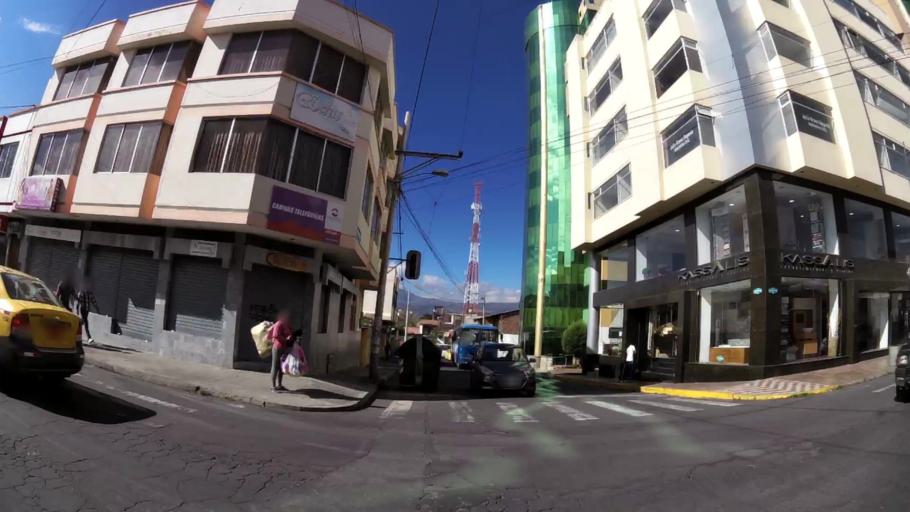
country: EC
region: Chimborazo
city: Riobamba
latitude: -1.6626
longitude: -78.6594
